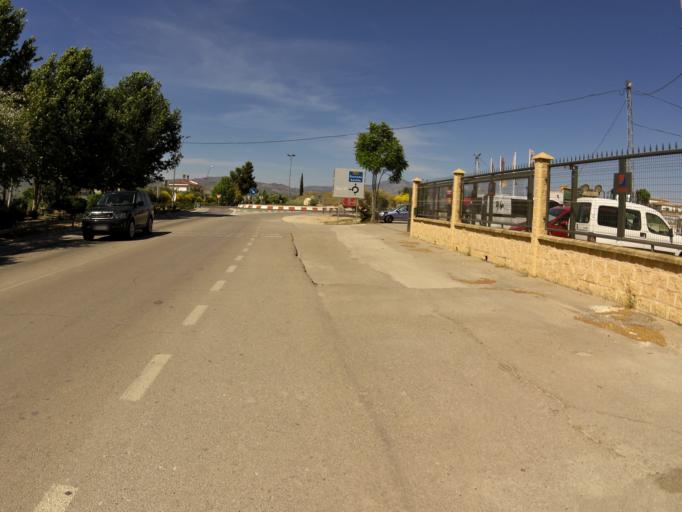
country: ES
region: Andalusia
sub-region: Provincia de Granada
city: Huetor-Tajar
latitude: 37.1880
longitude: -4.0332
